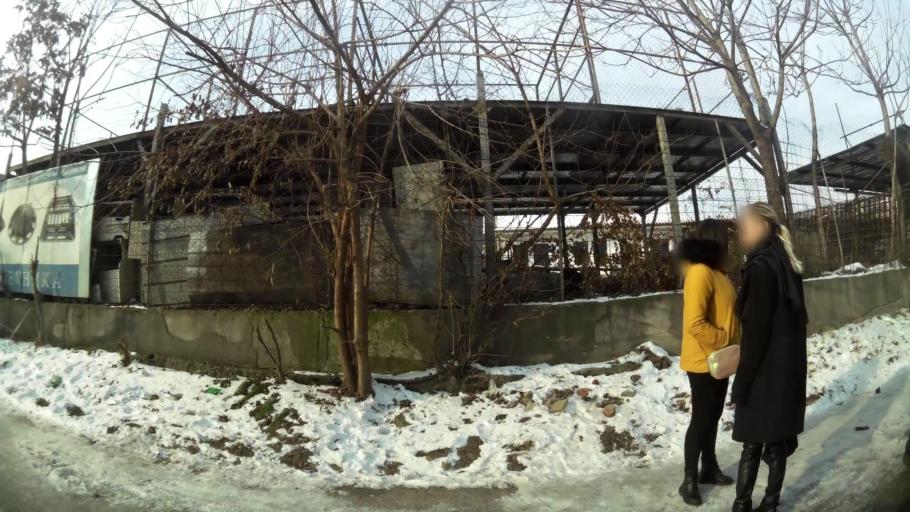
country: MK
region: Cair
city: Cair
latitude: 42.0129
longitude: 21.4316
